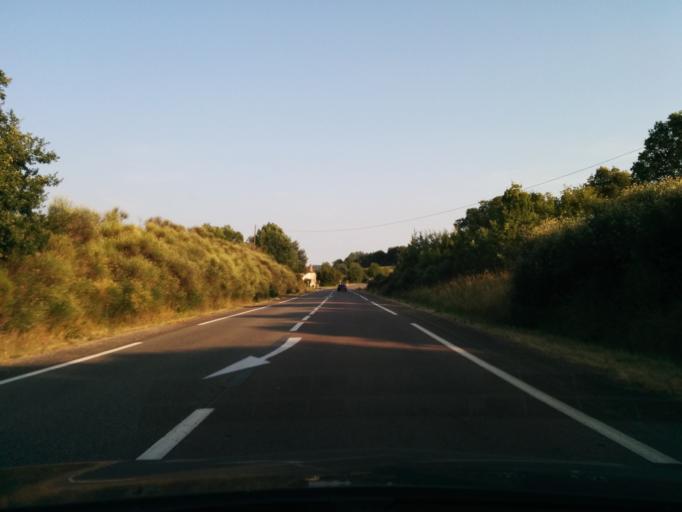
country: FR
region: Midi-Pyrenees
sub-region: Departement du Lot
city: Pradines
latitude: 44.5738
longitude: 1.4729
